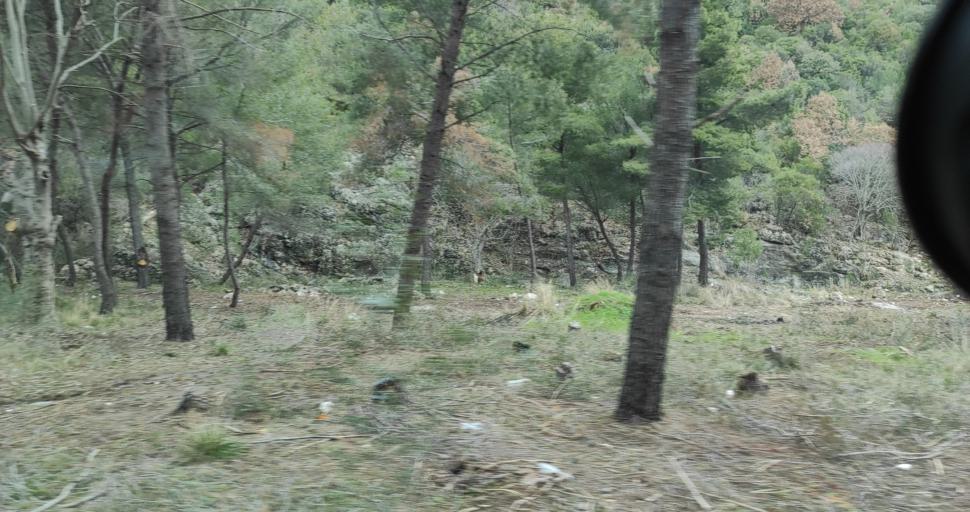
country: AL
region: Lezhe
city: Shengjin
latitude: 41.8234
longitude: 19.5607
